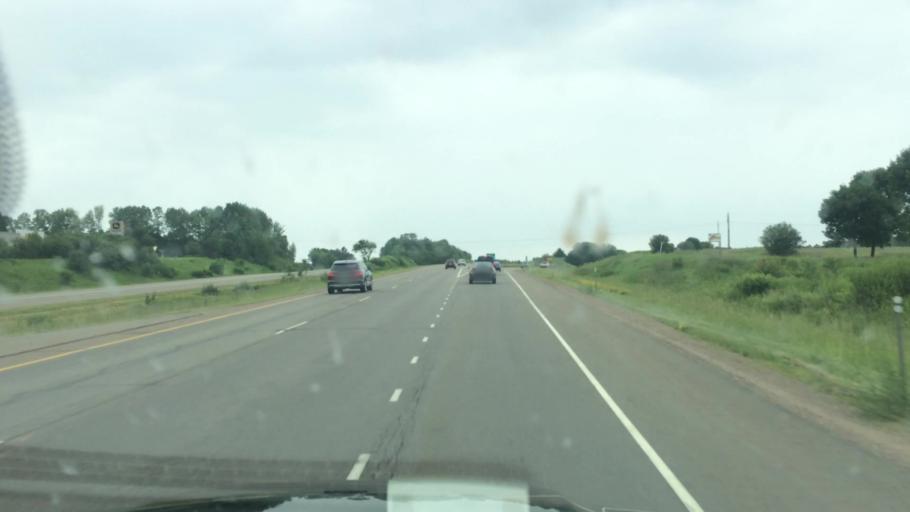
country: US
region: Wisconsin
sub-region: Lincoln County
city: Merrill
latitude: 45.1718
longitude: -89.6456
